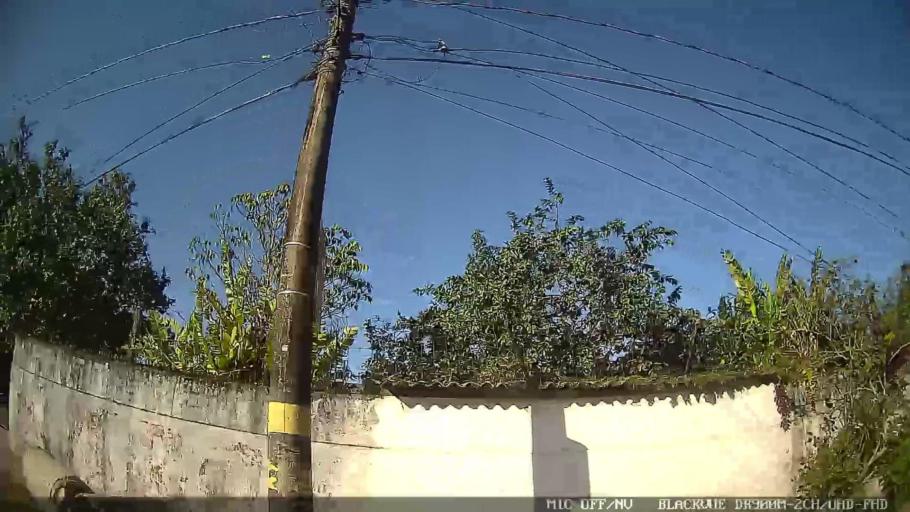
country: BR
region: Sao Paulo
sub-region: Guaruja
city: Guaruja
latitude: -23.9655
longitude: -46.2816
